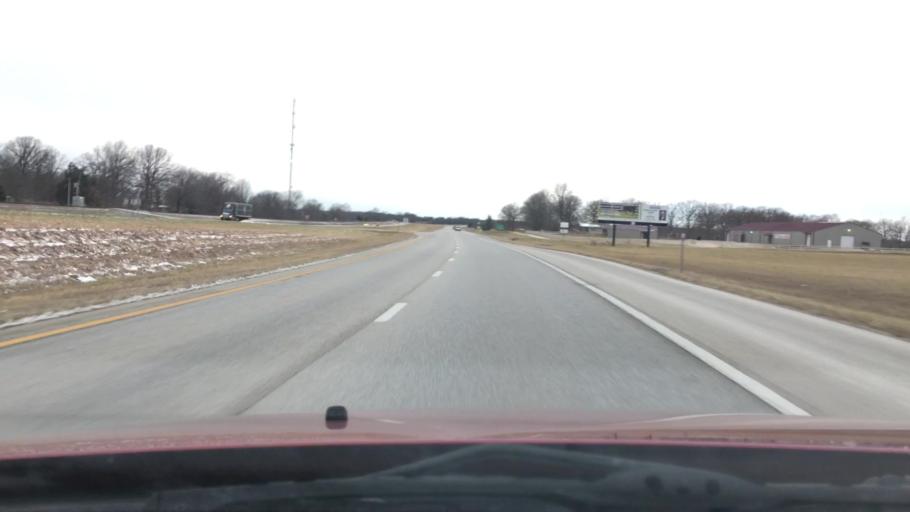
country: US
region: Missouri
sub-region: Webster County
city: Seymour
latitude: 37.1694
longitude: -92.8113
